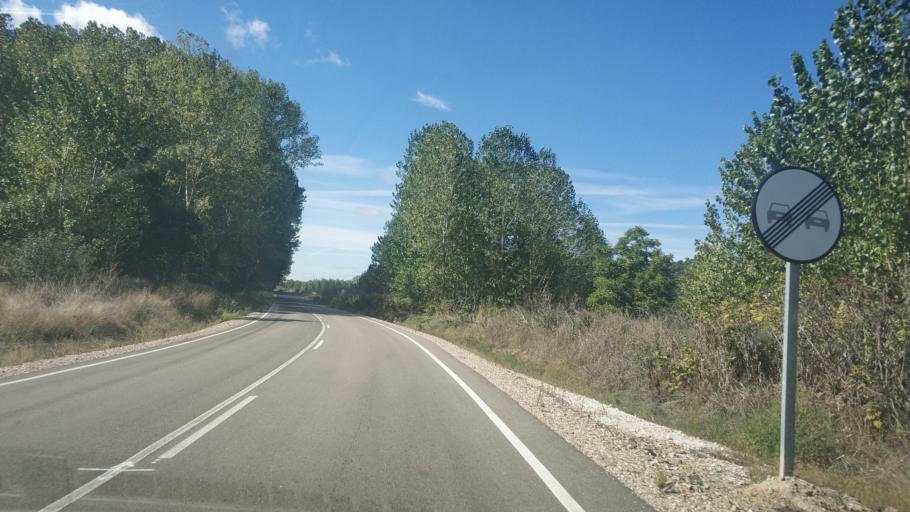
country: ES
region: Castille and Leon
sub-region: Provincia de Burgos
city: Puentedura
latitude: 42.0532
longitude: -3.5595
